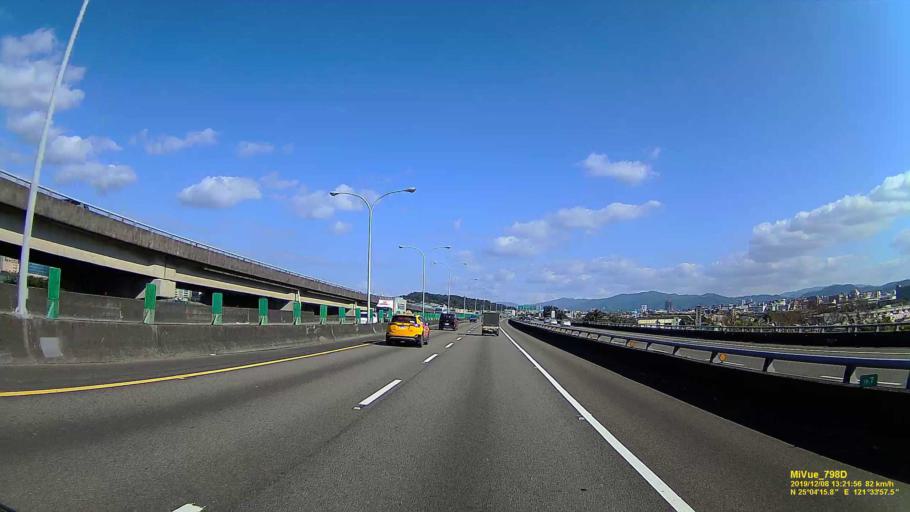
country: TW
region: Taipei
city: Taipei
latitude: 25.0713
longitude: 121.5643
